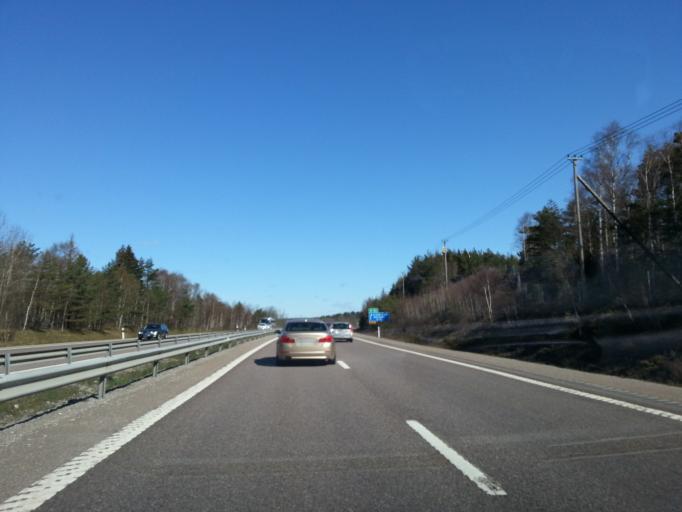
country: SE
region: Vaestra Goetaland
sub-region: Kungalvs Kommun
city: Kode
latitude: 57.9695
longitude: 11.8404
